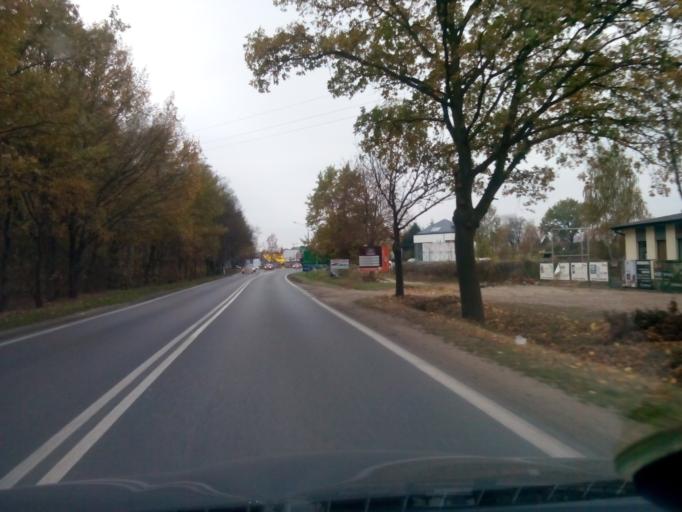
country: PL
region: Masovian Voivodeship
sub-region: Powiat pruszkowski
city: Otrebusy
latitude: 52.1321
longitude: 20.7590
